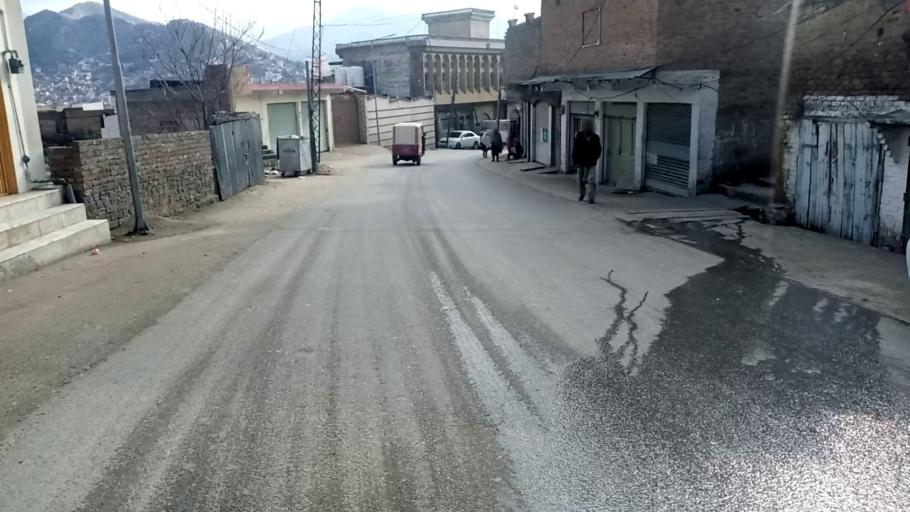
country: PK
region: Khyber Pakhtunkhwa
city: Mingora
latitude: 34.7742
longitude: 72.3681
